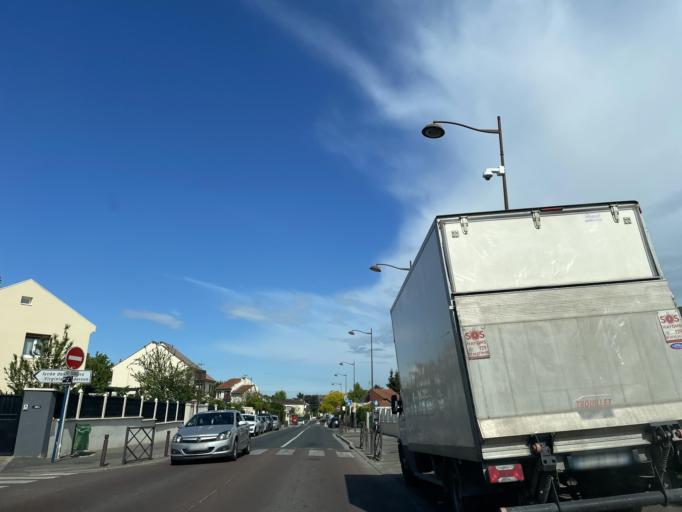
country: FR
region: Ile-de-France
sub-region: Departement du Val-d'Oise
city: Arnouville
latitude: 48.9854
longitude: 2.4073
